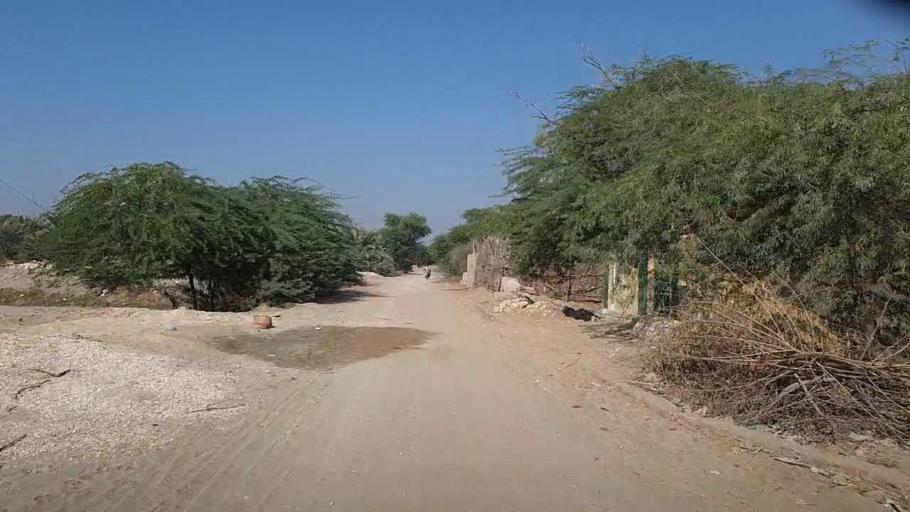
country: PK
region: Sindh
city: Bozdar
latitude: 27.1927
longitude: 68.6688
